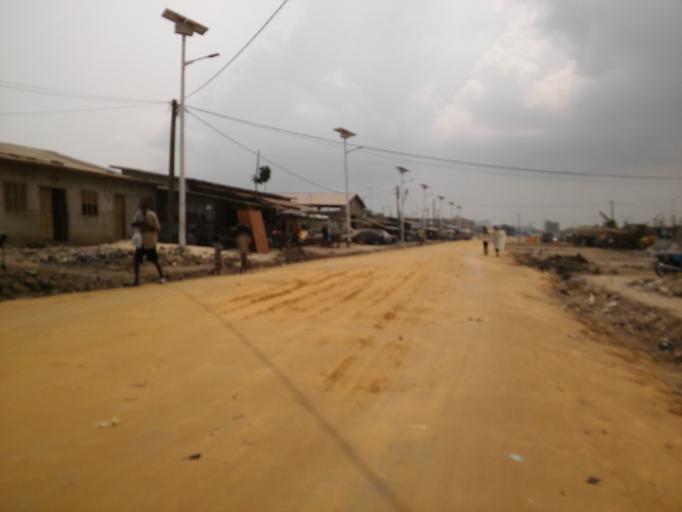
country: BJ
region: Littoral
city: Cotonou
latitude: 6.3909
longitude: 2.4110
